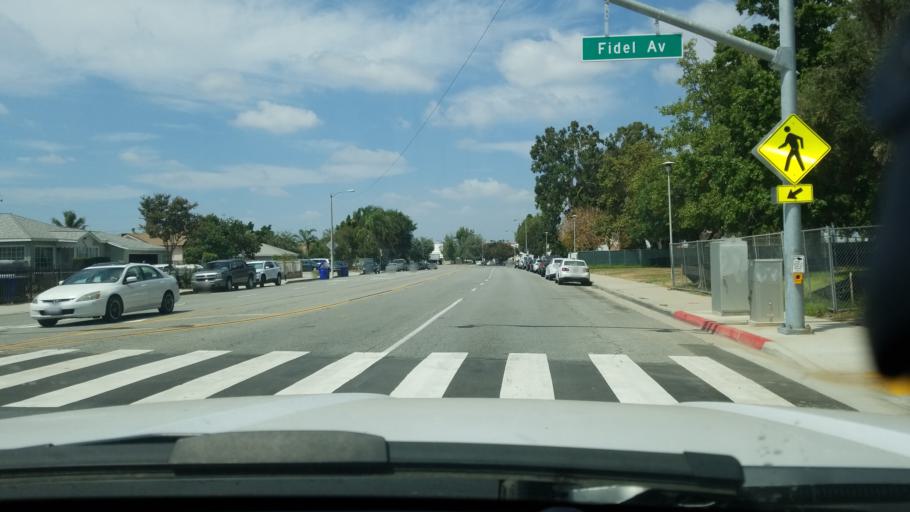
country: US
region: California
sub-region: Los Angeles County
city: South Whittier
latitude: 33.9288
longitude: -118.0506
